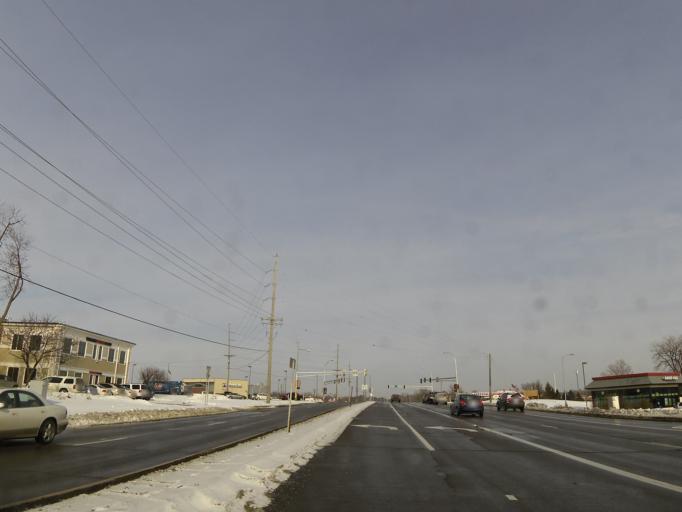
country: US
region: Minnesota
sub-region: Hennepin County
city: Minnetonka
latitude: 44.9125
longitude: -93.5033
